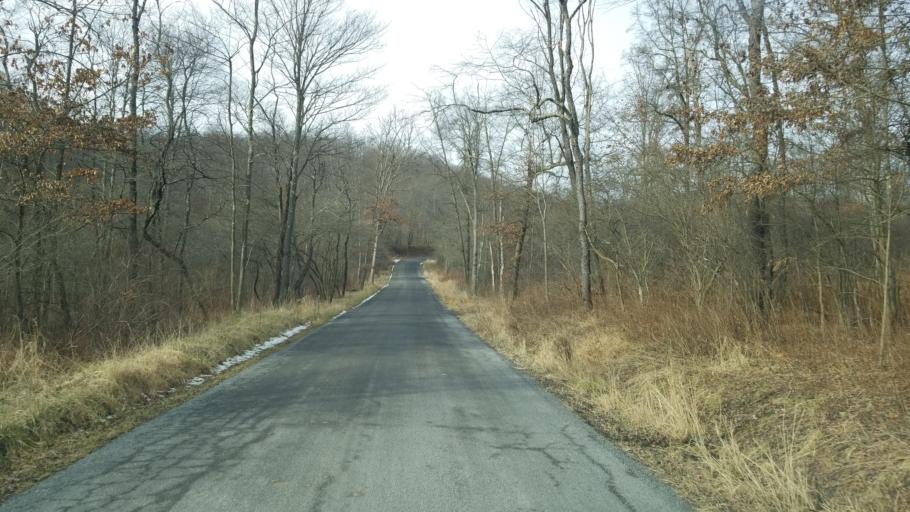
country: US
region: Pennsylvania
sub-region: Jefferson County
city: Punxsutawney
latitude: 40.8698
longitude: -79.0502
